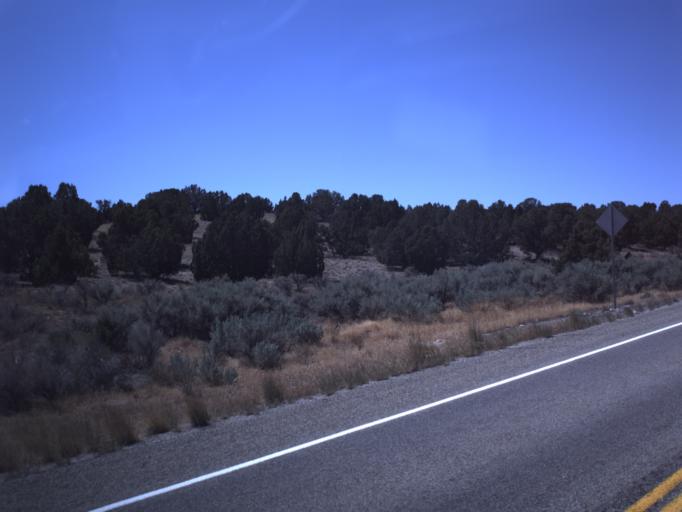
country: US
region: Utah
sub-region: Juab County
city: Nephi
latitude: 39.6656
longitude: -112.0423
